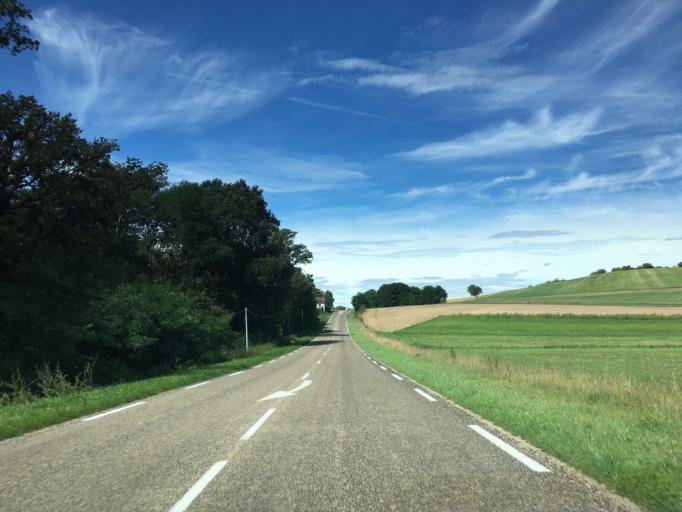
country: FR
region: Bourgogne
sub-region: Departement de l'Yonne
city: Charbuy
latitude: 47.8219
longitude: 3.4360
